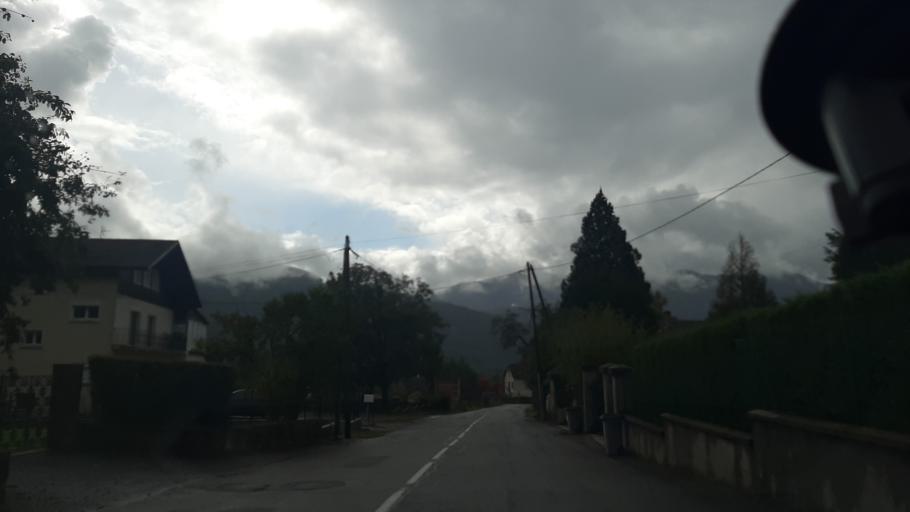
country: FR
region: Rhone-Alpes
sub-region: Departement de la Savoie
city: Gresy-sur-Isere
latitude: 45.5976
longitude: 6.2590
